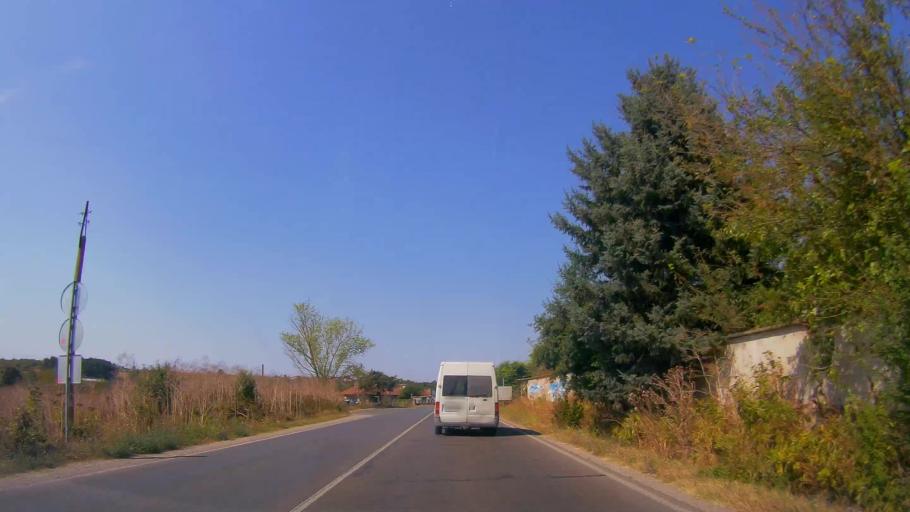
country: BG
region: Razgrad
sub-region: Obshtina Tsar Kaloyan
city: Tsar Kaloyan
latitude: 43.5999
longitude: 26.2465
